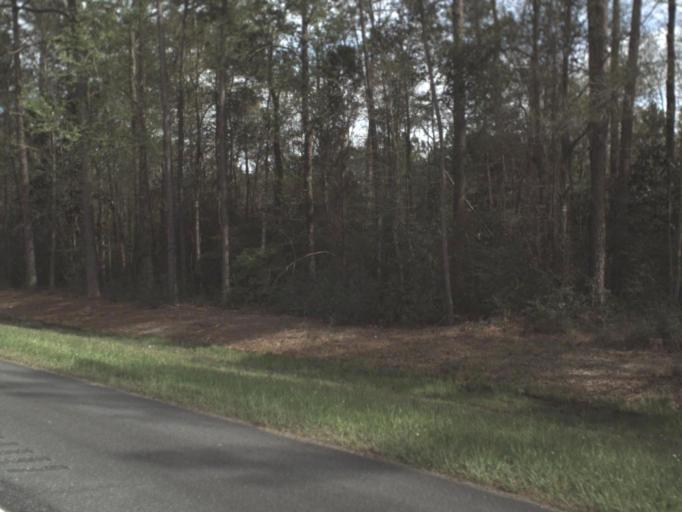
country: US
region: Florida
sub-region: Walton County
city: DeFuniak Springs
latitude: 30.6913
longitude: -86.0996
